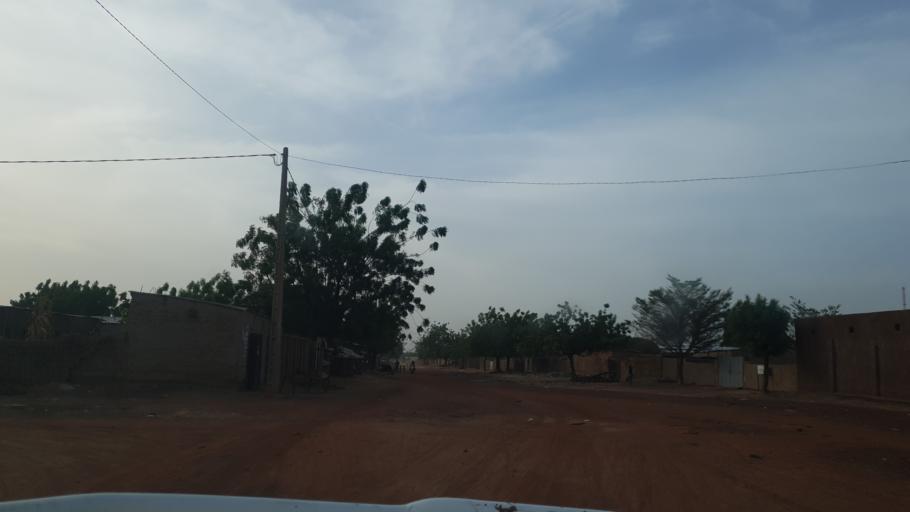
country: ML
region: Segou
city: Baroueli
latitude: 12.7804
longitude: -6.9440
